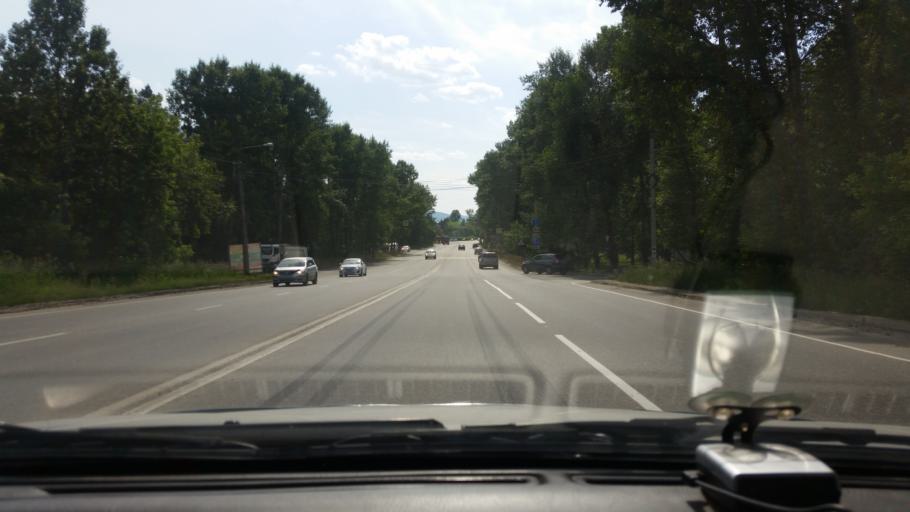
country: RU
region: Irkutsk
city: Shelekhov
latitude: 52.2093
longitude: 104.1039
